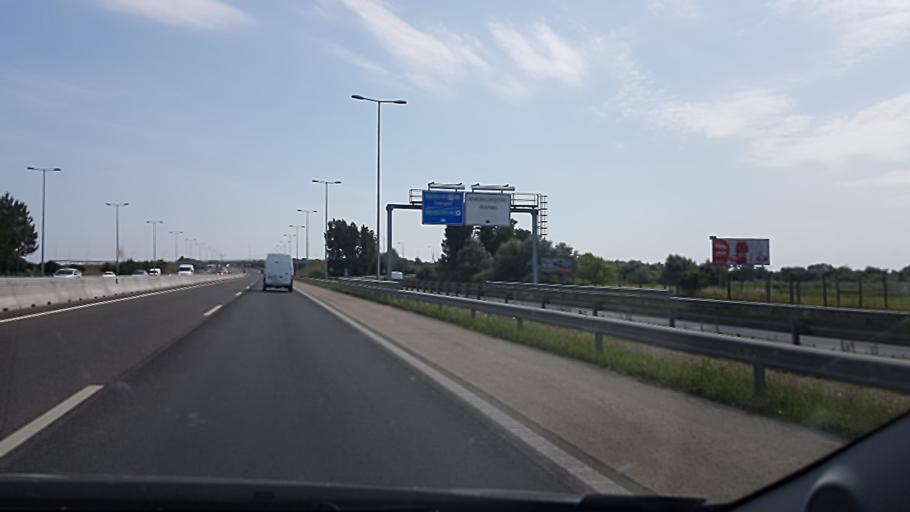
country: HU
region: Budapest
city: Budapest XVIII. keruelet
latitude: 47.4184
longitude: 19.1538
